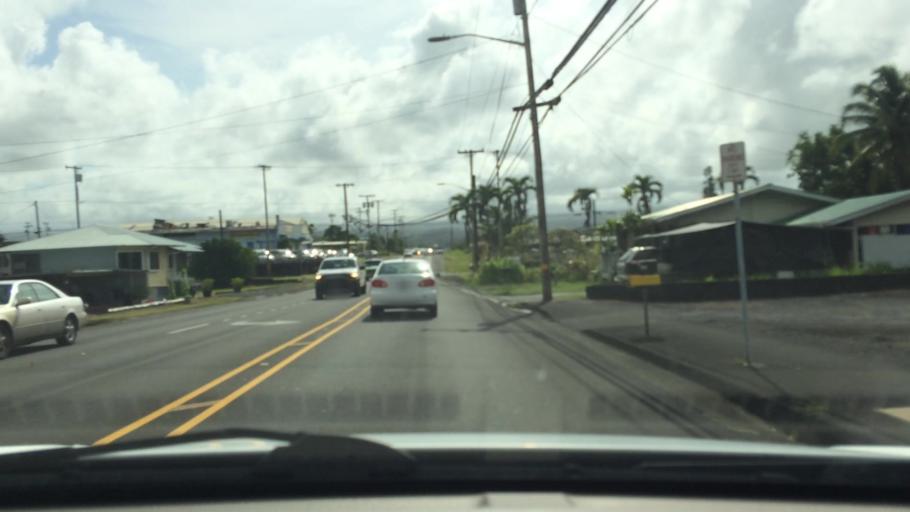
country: US
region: Hawaii
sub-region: Hawaii County
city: Hilo
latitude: 19.7118
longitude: -155.0705
